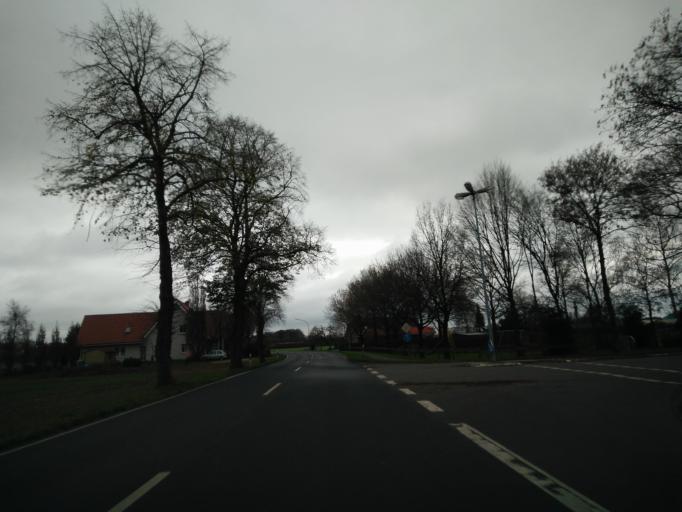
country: NL
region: Drenthe
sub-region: Gemeente Emmen
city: Emmer-Compascuum
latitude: 52.8224
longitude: 7.1129
